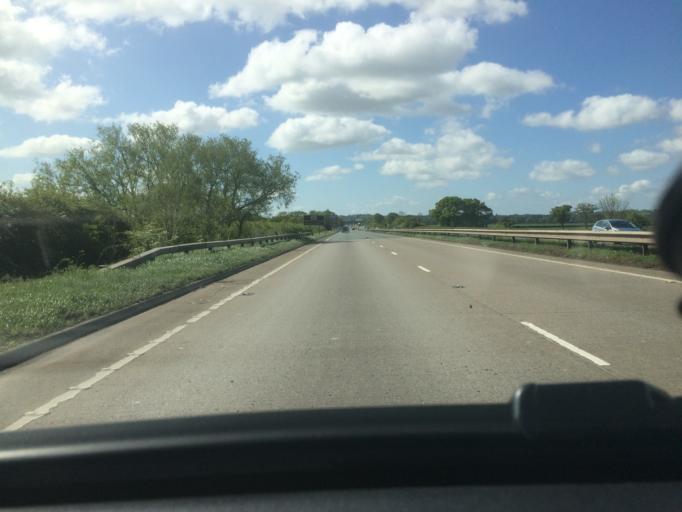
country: GB
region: Wales
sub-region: Wrexham
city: Rossett
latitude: 53.1287
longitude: -2.9480
